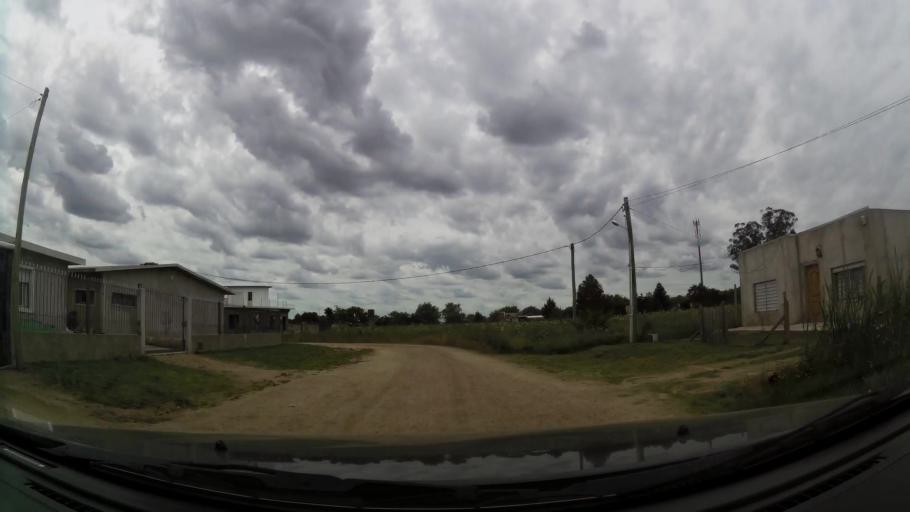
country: UY
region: Canelones
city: Las Piedras
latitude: -34.7211
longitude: -56.2024
